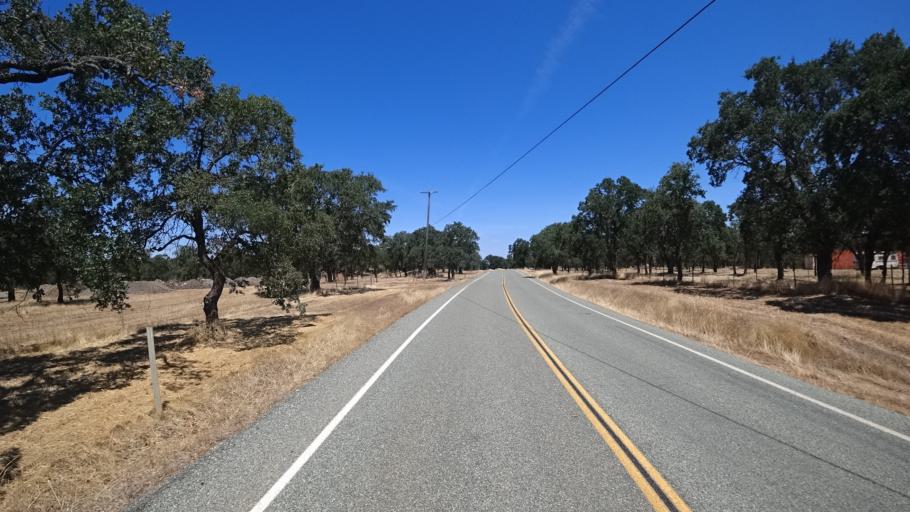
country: US
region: California
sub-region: Calaveras County
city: Rancho Calaveras
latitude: 38.2031
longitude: -120.9466
